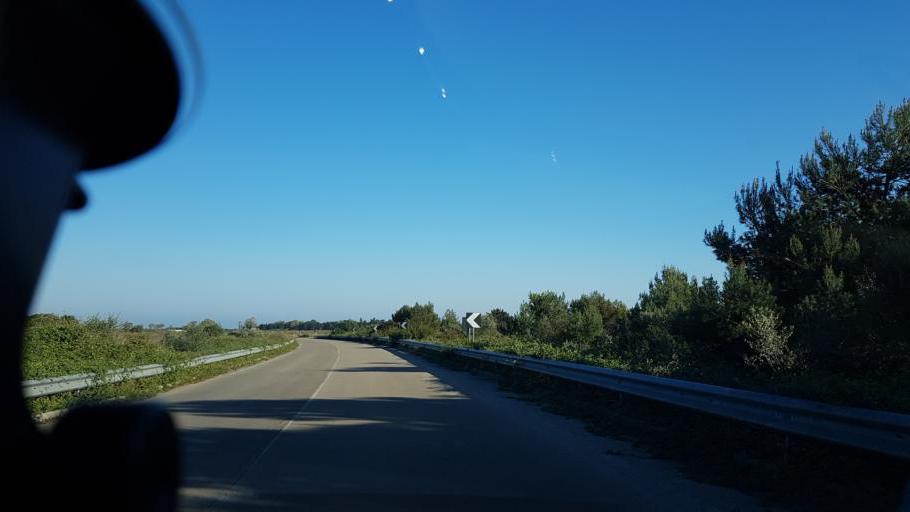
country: IT
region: Apulia
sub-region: Provincia di Lecce
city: Merine
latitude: 40.3951
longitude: 18.2550
